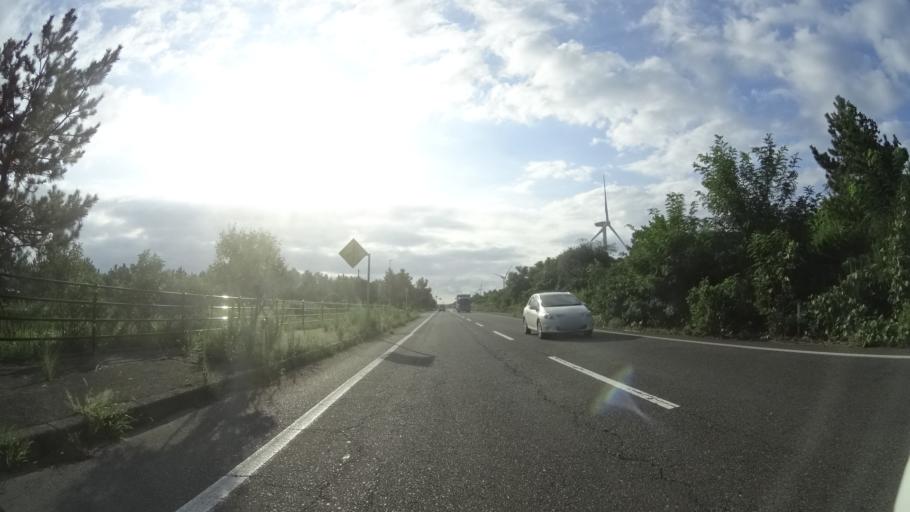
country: JP
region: Tottori
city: Kurayoshi
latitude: 35.4959
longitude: 133.8396
